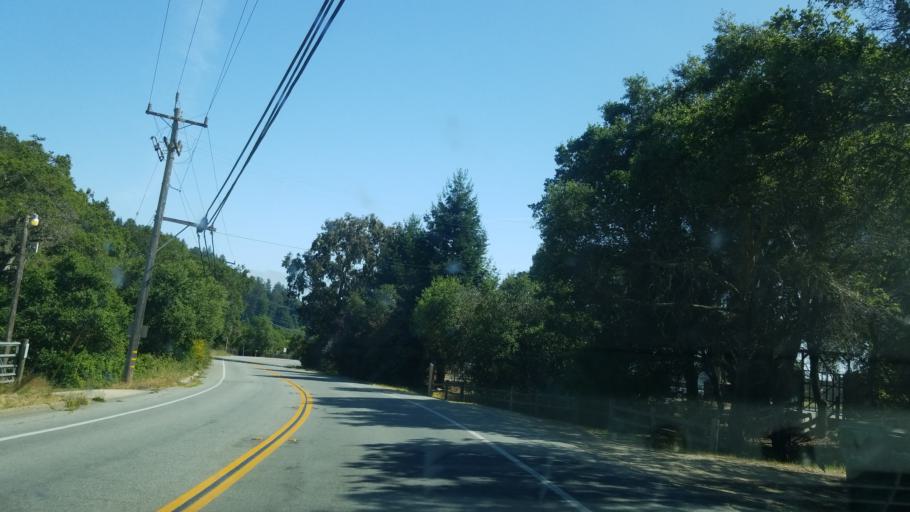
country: US
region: California
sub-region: Santa Cruz County
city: Soquel
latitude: 37.0173
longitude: -121.9525
